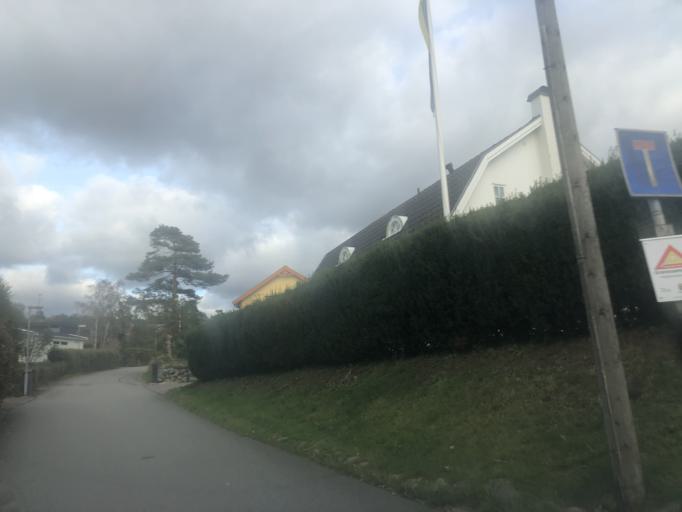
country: SE
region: Vaestra Goetaland
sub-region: Goteborg
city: Billdal
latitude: 57.6296
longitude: 11.9475
